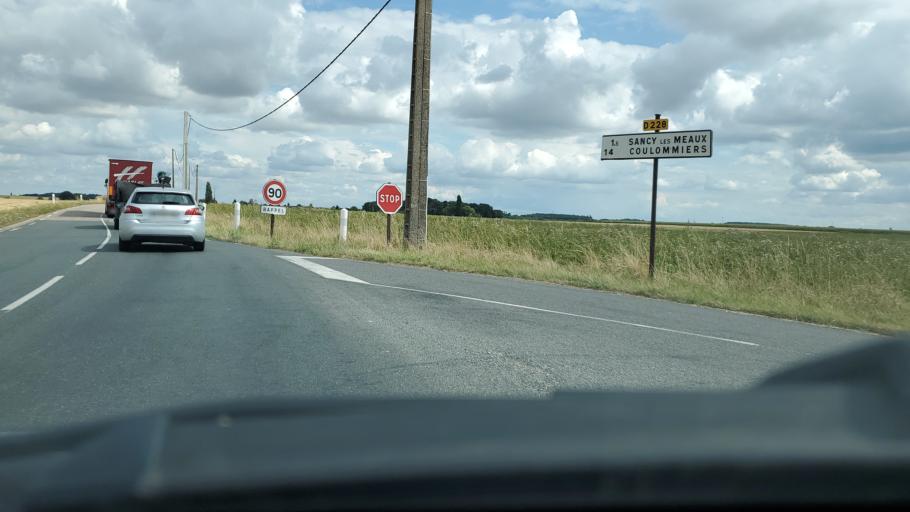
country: FR
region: Ile-de-France
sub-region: Departement de Seine-et-Marne
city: Bouleurs
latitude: 48.8921
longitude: 2.9431
